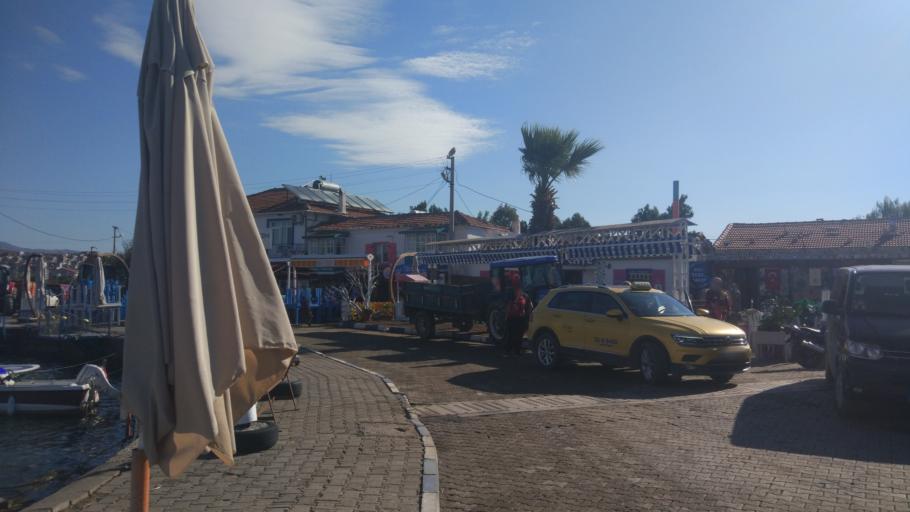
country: TR
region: Izmir
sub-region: Seferihisar
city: Seferhisar
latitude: 38.1955
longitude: 26.7862
